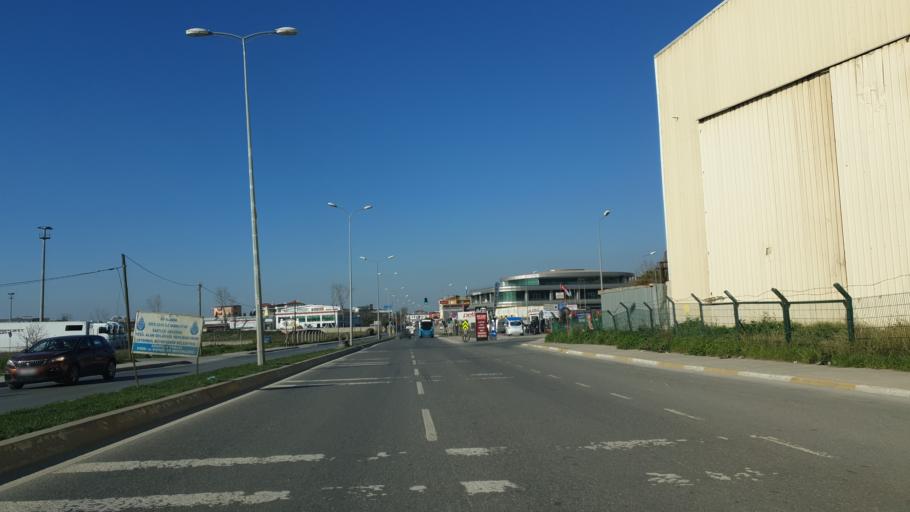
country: TR
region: Istanbul
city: Icmeler
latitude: 40.8879
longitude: 29.3528
